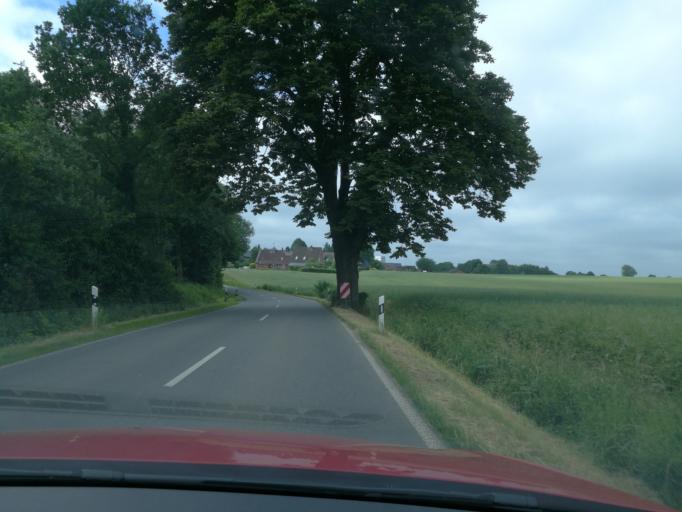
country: DE
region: Schleswig-Holstein
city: Lasbek
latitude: 53.7482
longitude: 10.3796
